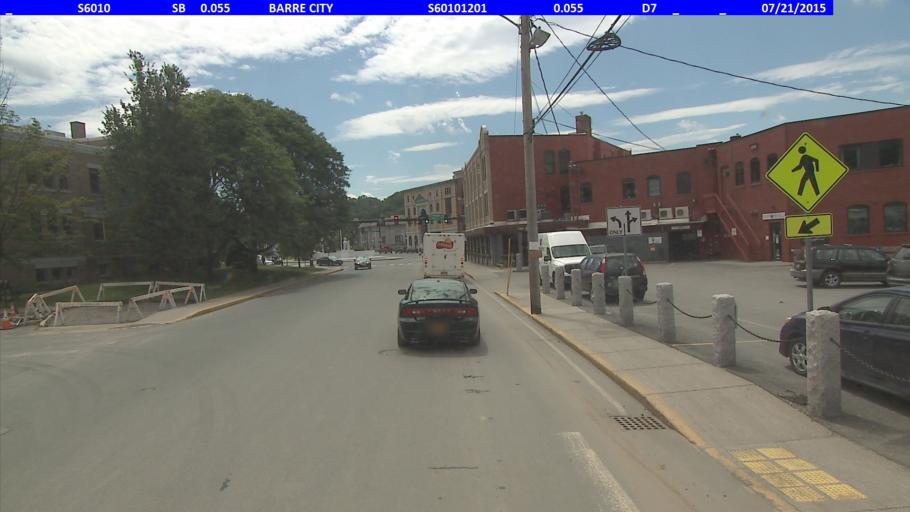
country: US
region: Vermont
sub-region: Washington County
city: Barre
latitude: 44.1981
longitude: -72.5011
